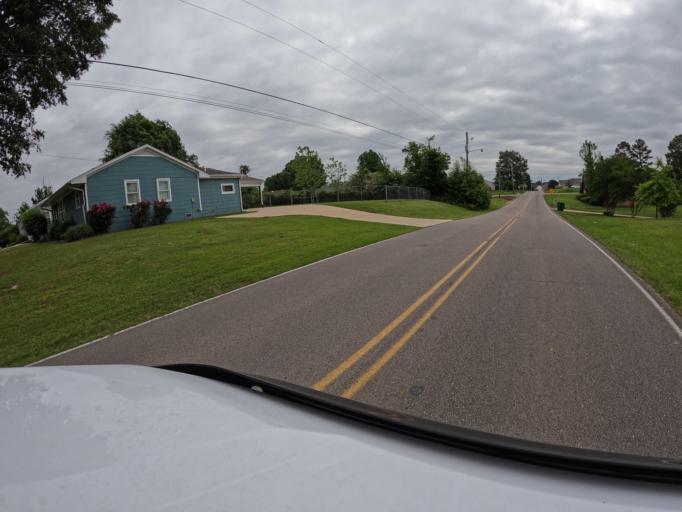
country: US
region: Mississippi
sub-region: Lee County
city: Tupelo
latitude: 34.2776
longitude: -88.7294
